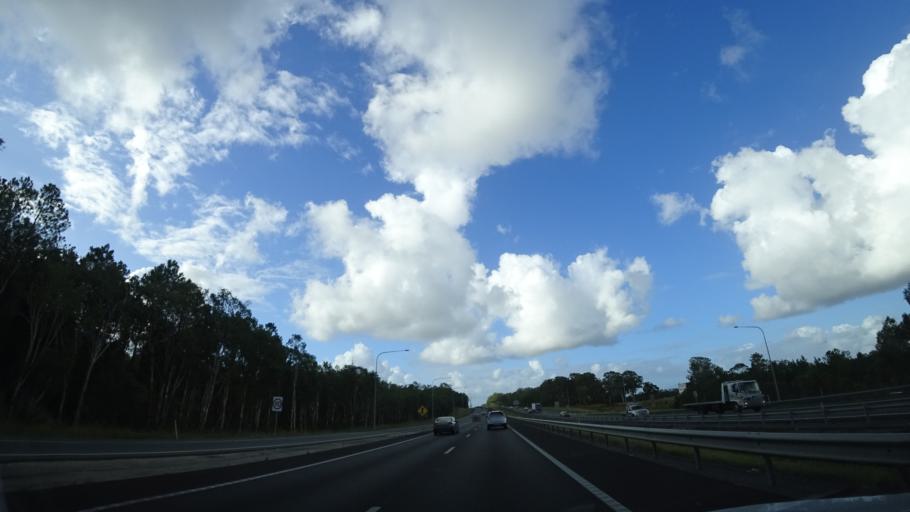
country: AU
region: Queensland
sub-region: Moreton Bay
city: Caboolture
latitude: -27.0364
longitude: 152.9779
